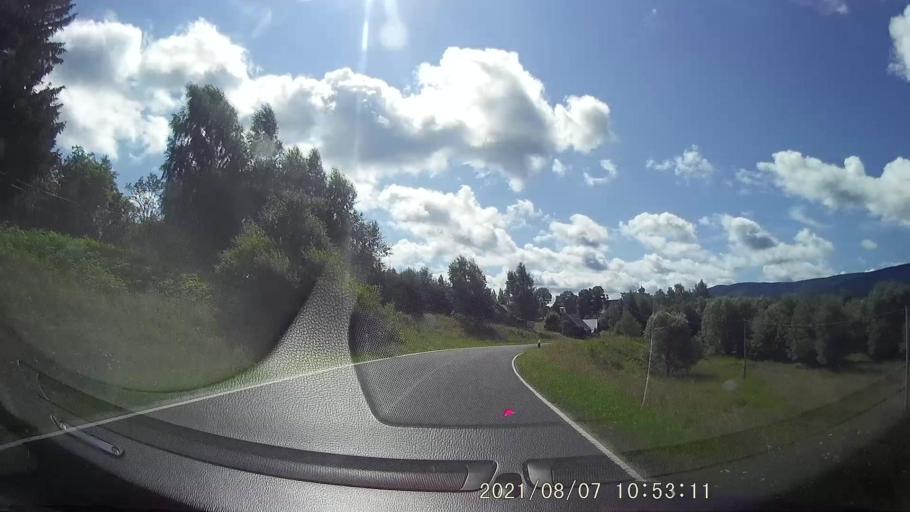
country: CZ
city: Rokytnice v Orlickych Horach
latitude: 50.2775
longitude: 16.4806
